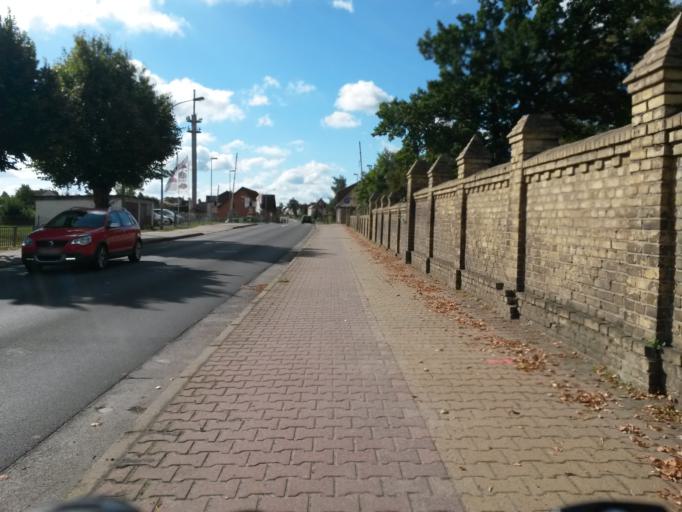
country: DE
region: Brandenburg
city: Templin
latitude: 53.1161
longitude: 13.4983
